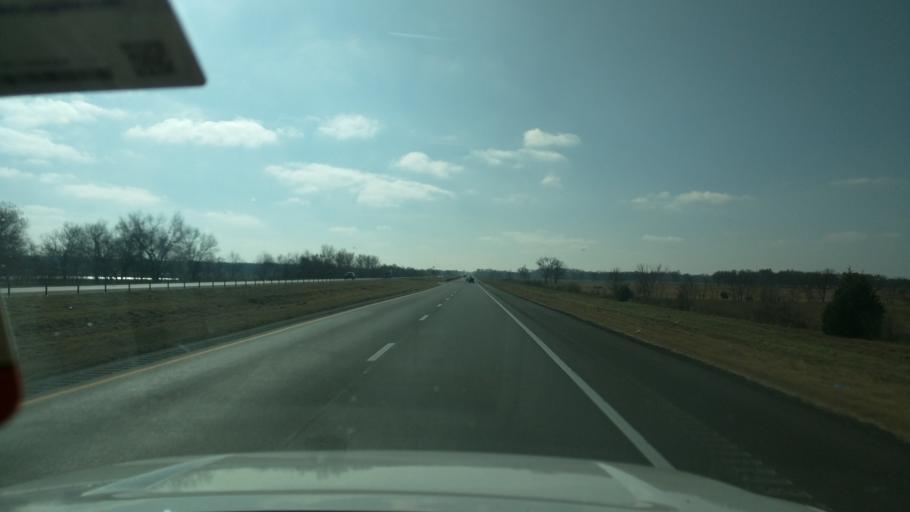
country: US
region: Oklahoma
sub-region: Washington County
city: Bartlesville
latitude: 36.6649
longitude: -95.9356
